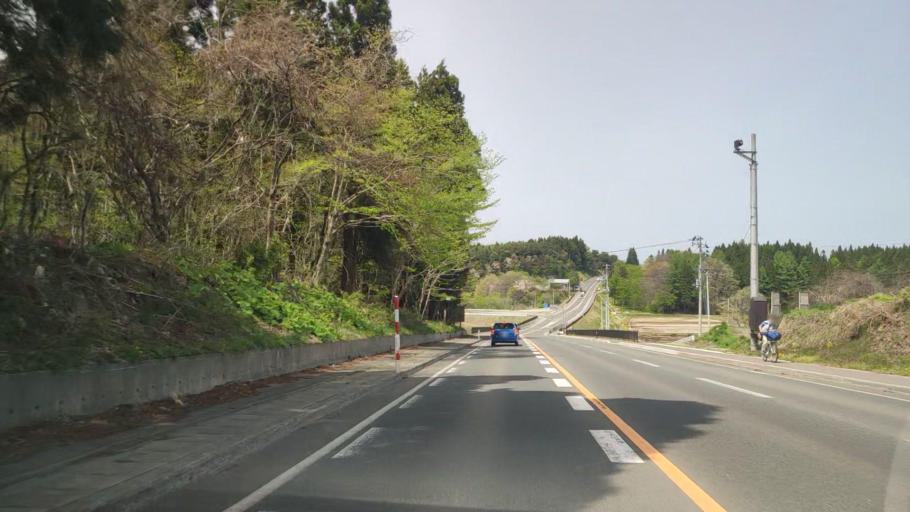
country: JP
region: Aomori
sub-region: Misawa Shi
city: Inuotose
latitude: 40.6621
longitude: 141.1889
